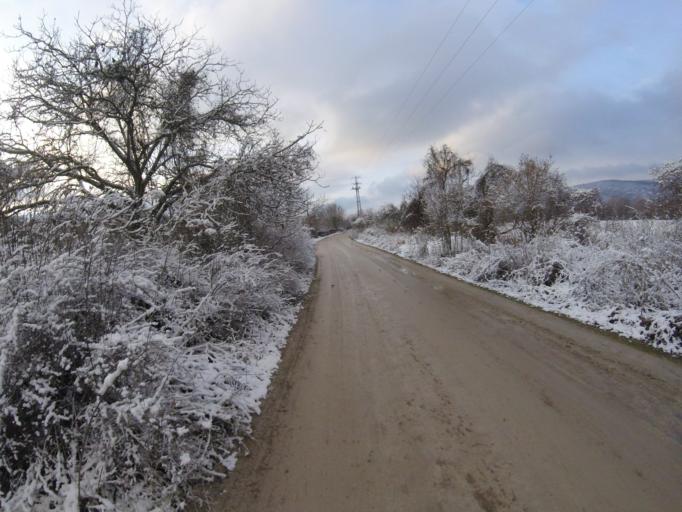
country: HU
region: Komarom-Esztergom
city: Esztergom
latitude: 47.8014
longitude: 18.7779
